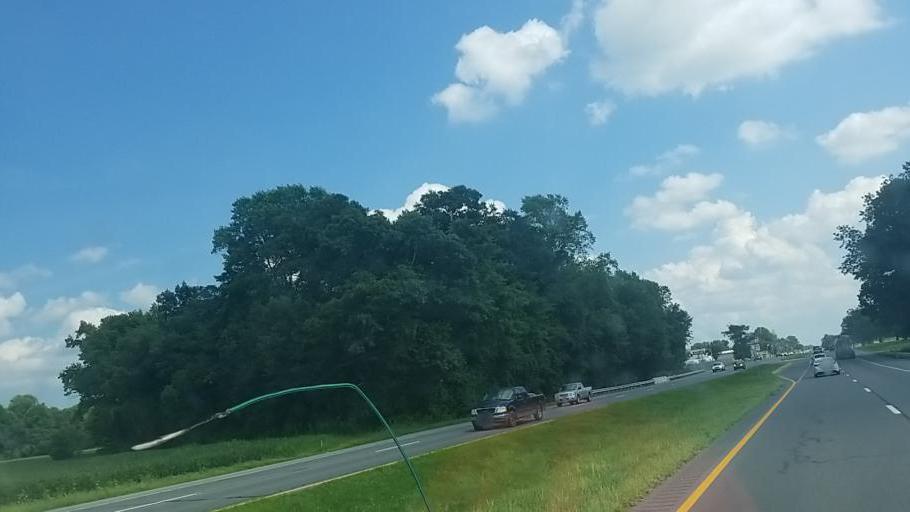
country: US
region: Delaware
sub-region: Sussex County
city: Georgetown
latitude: 38.6405
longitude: -75.3564
